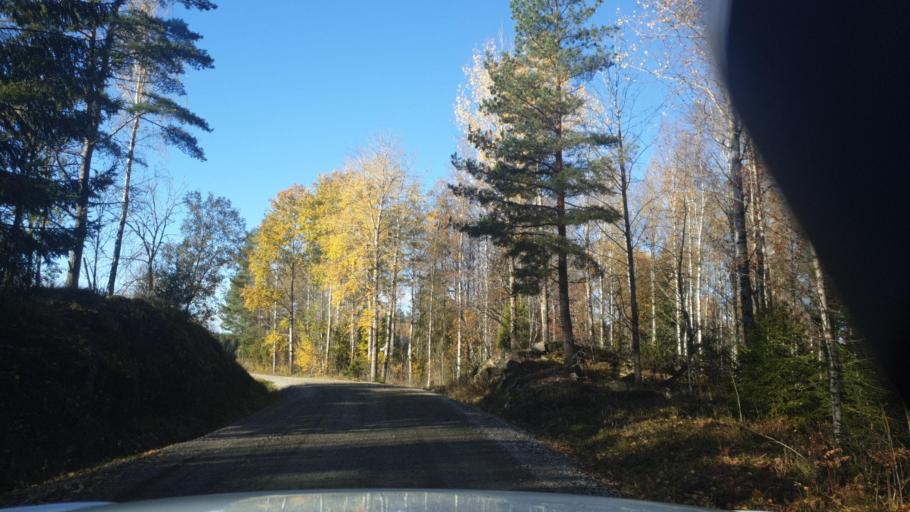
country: SE
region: Vaermland
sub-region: Arvika Kommun
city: Arvika
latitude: 59.5934
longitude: 12.8059
